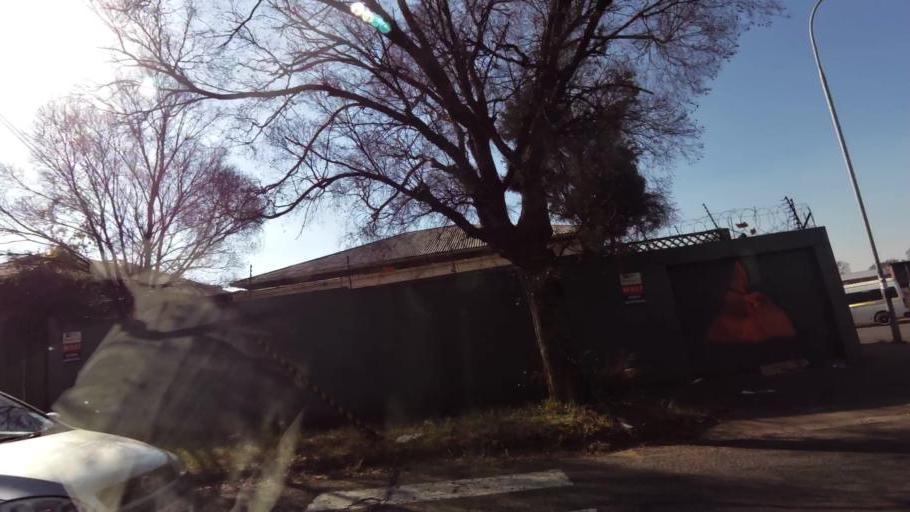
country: ZA
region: Gauteng
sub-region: City of Johannesburg Metropolitan Municipality
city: Johannesburg
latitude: -26.1735
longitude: 27.9625
